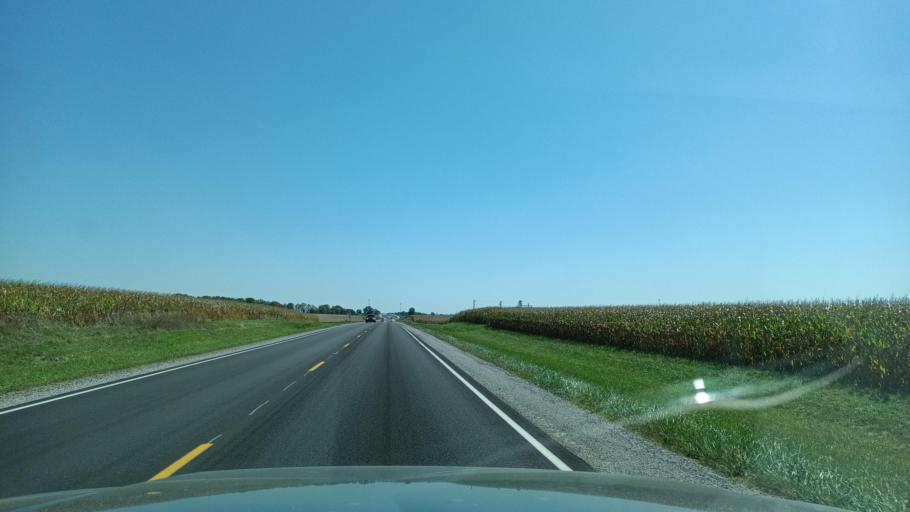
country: US
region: Illinois
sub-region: McLean County
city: Twin Grove
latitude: 40.5484
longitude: -89.0707
